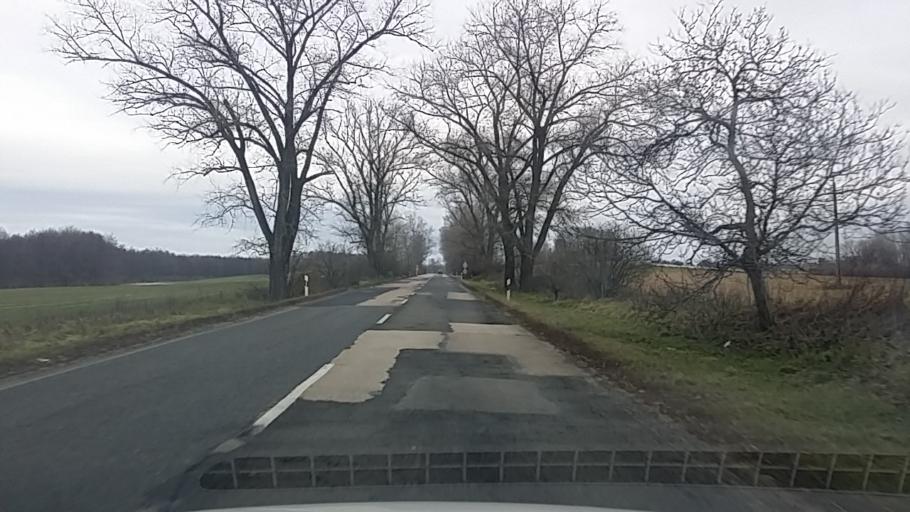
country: HU
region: Komarom-Esztergom
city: Csaszar
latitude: 47.4279
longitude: 18.1291
